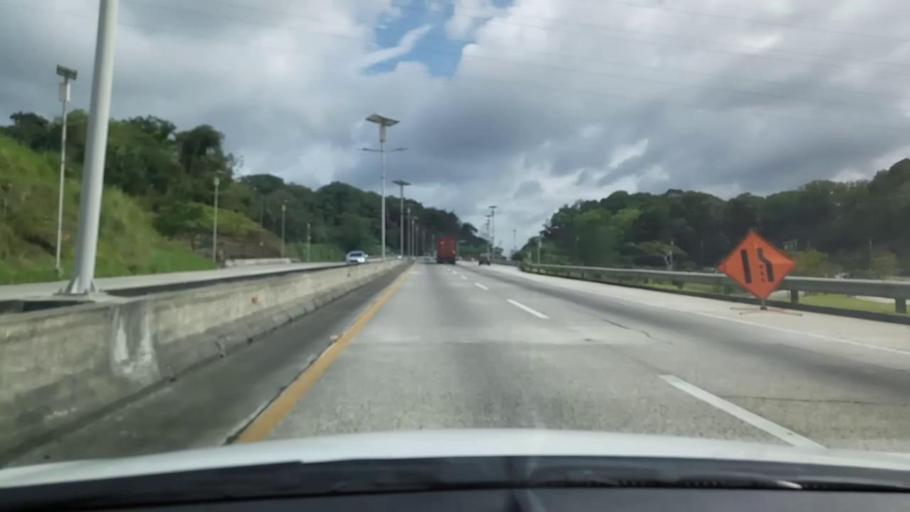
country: PA
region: Panama
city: Chilibre
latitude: 9.1252
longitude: -79.6198
